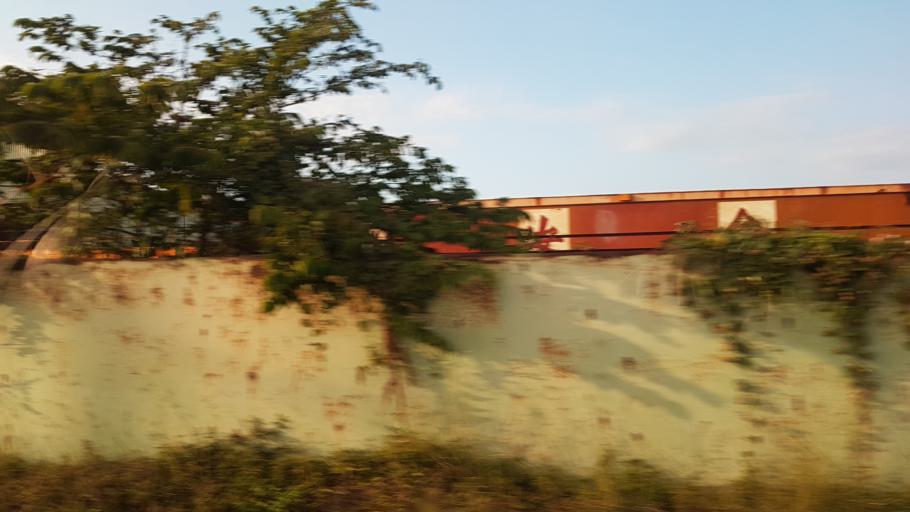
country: TW
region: Taiwan
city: Xinying
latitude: 23.3438
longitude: 120.3481
